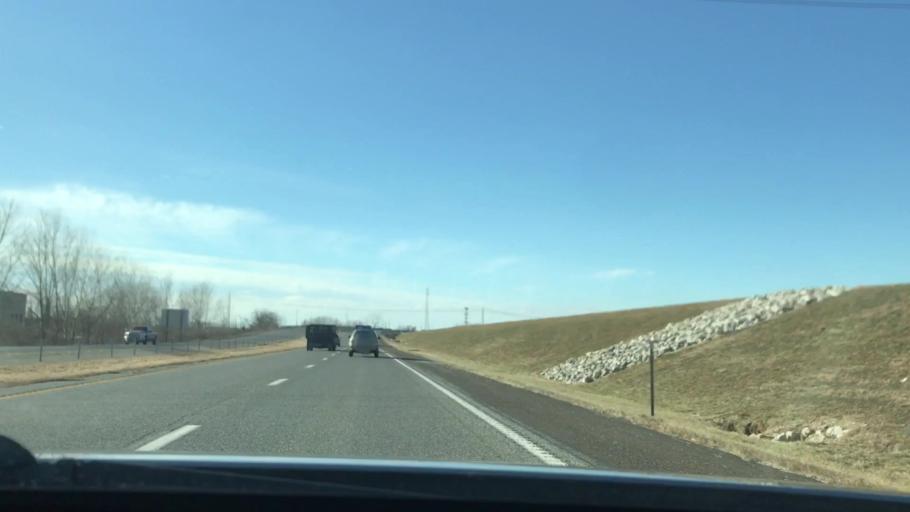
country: US
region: Missouri
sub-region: Platte County
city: Riverside
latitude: 39.1659
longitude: -94.6093
